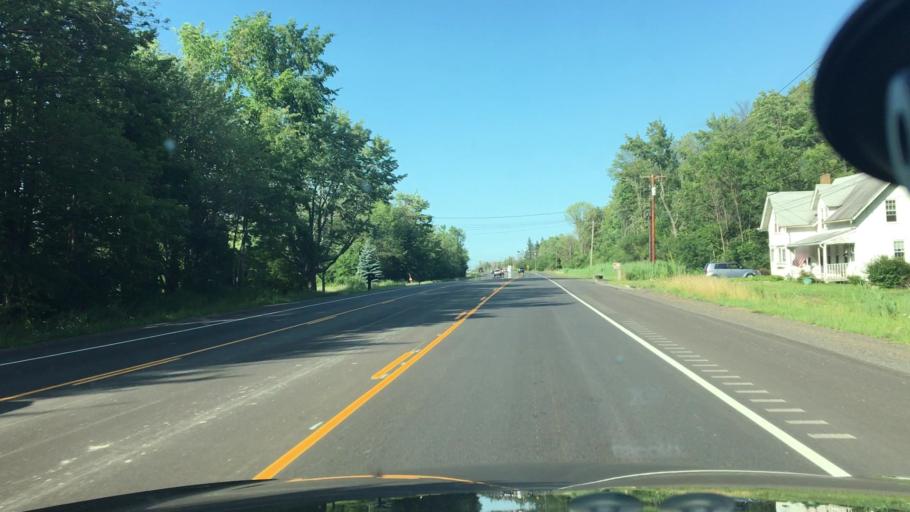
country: US
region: New York
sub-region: Erie County
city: Wanakah
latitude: 42.7230
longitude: -78.8959
